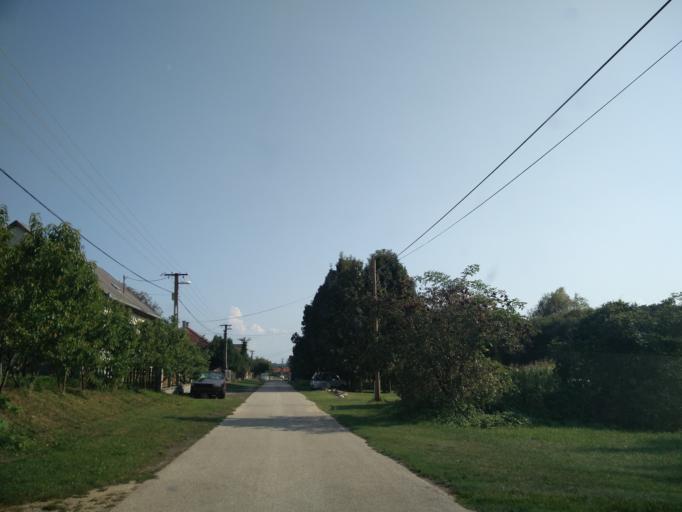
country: HU
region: Zala
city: Zalaegerszeg
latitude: 46.8690
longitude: 16.8493
